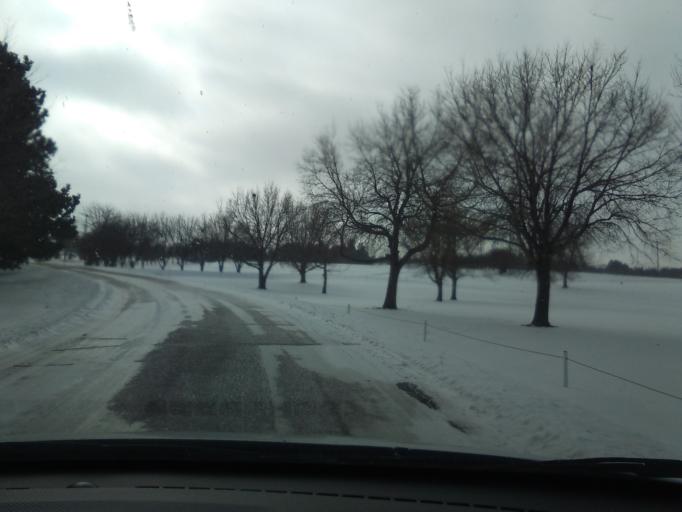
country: US
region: Nebraska
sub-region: Kimball County
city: Kimball
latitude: 41.2280
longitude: -103.6169
